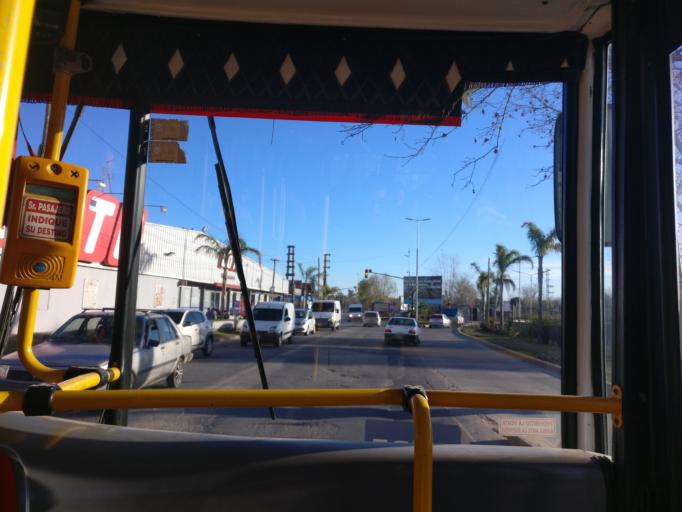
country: AR
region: Buenos Aires
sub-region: Partido de Ezeiza
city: Ezeiza
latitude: -34.8929
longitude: -58.5716
